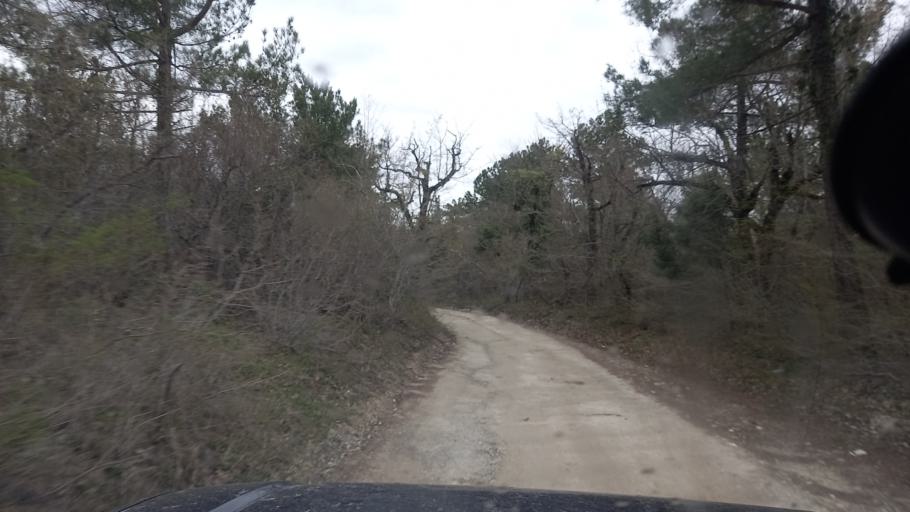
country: RU
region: Krasnodarskiy
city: Dzhubga
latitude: 44.3196
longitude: 38.6877
